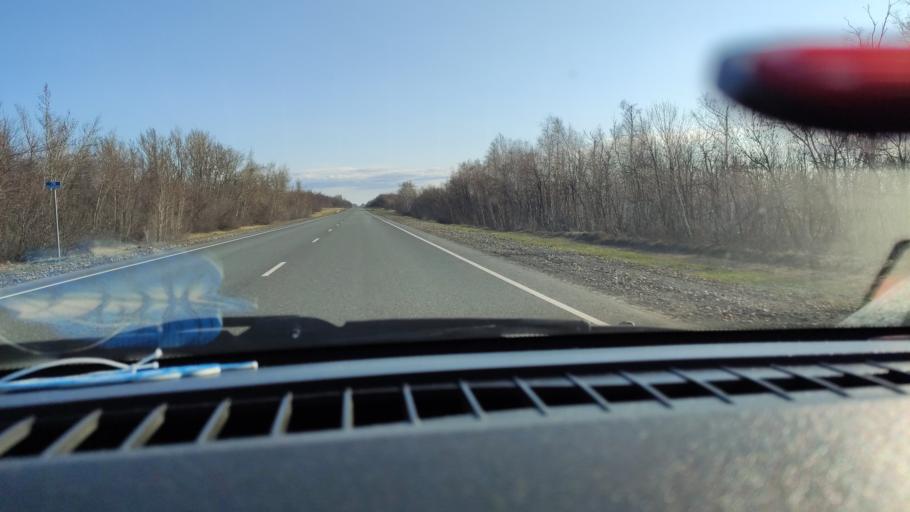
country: RU
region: Saratov
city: Khvalynsk
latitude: 52.5908
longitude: 48.1305
